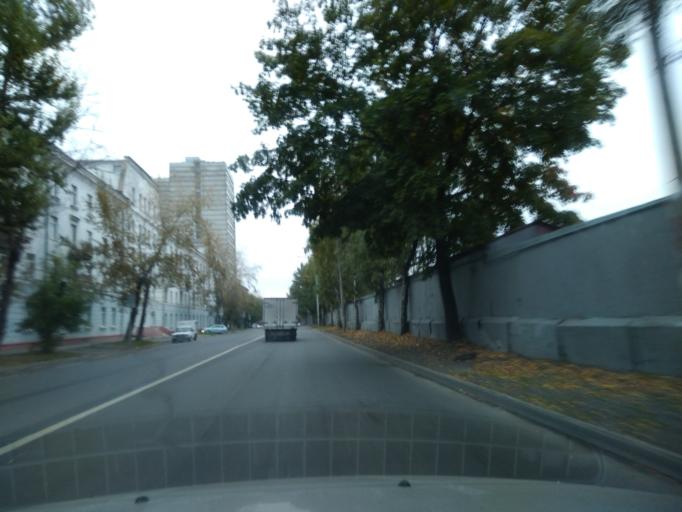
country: RU
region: Moscow
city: Sokol
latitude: 55.8063
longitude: 37.4934
